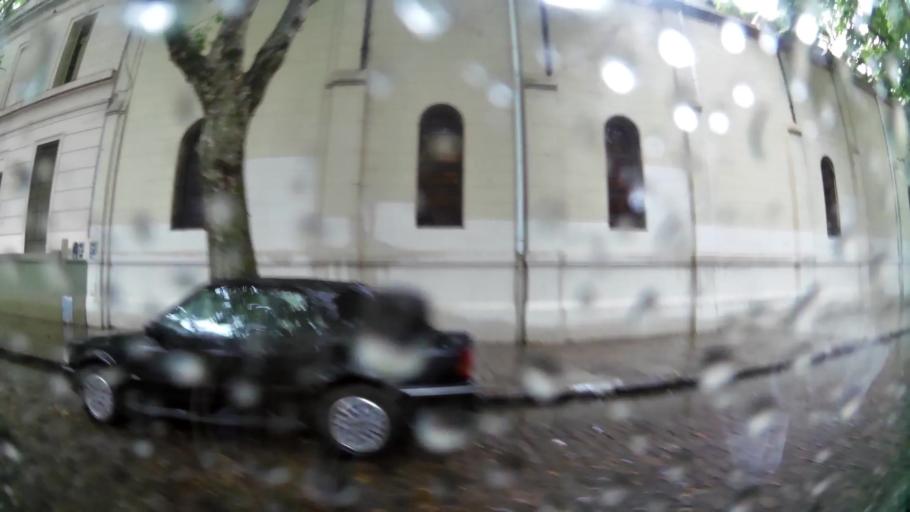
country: AR
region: Buenos Aires F.D.
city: Colegiales
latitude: -34.5933
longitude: -58.4362
